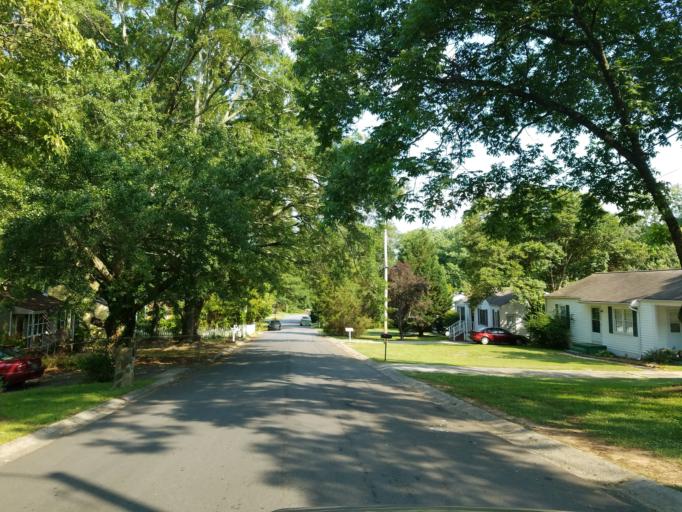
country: US
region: Georgia
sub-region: Cobb County
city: Marietta
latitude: 33.9470
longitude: -84.4964
